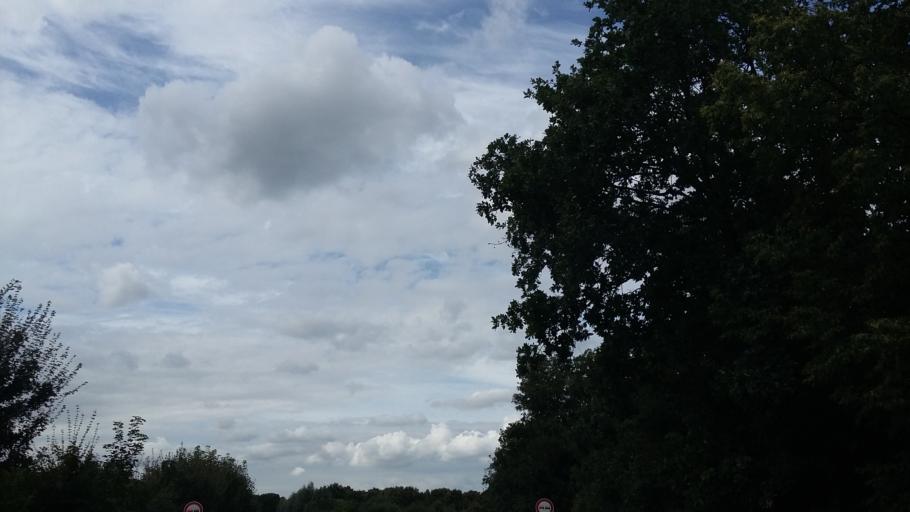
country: DE
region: Lower Saxony
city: Laatzen
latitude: 52.3074
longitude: 9.8278
